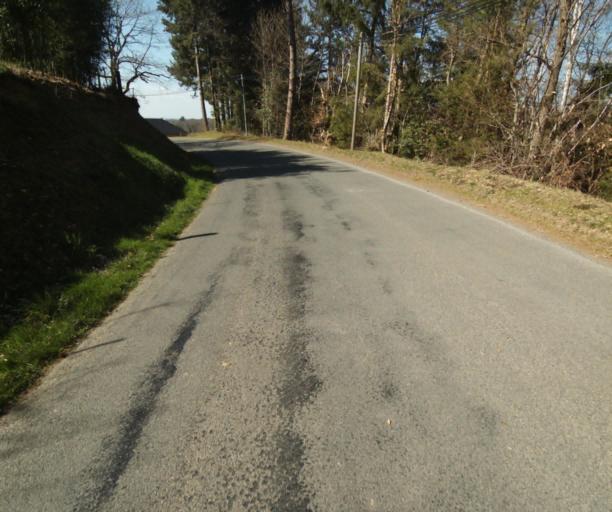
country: FR
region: Limousin
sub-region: Departement de la Correze
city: Saint-Mexant
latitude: 45.2970
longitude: 1.6893
